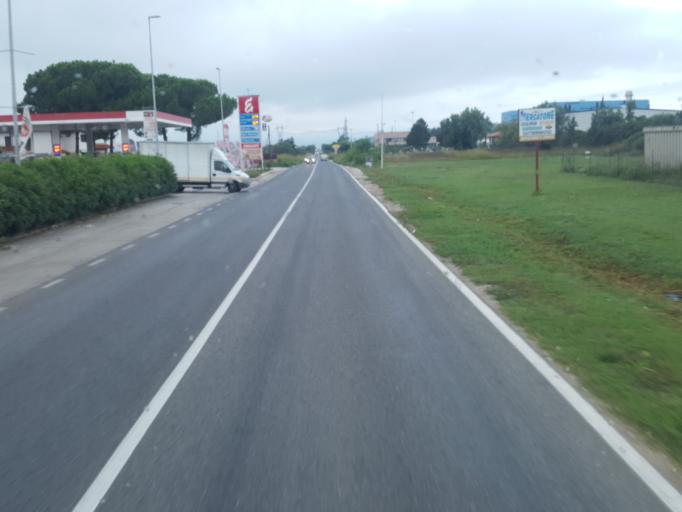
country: IT
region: Campania
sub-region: Provincia di Caserta
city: Sparanise
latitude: 41.1755
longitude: 14.1225
